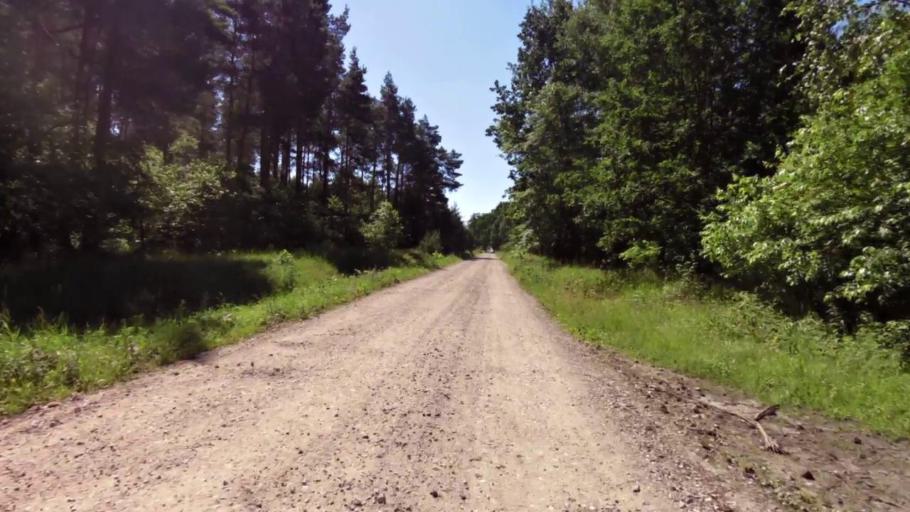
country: PL
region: West Pomeranian Voivodeship
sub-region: Powiat swidwinski
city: Rabino
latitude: 53.8966
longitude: 16.0091
